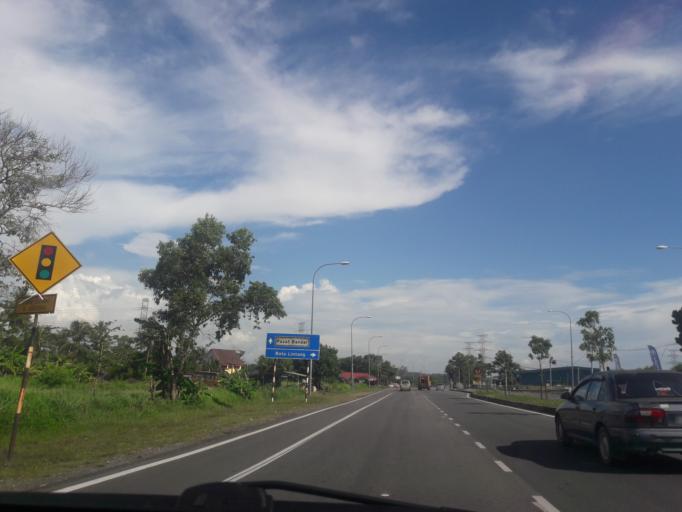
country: MY
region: Kedah
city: Sungai Petani
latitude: 5.6190
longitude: 100.4658
